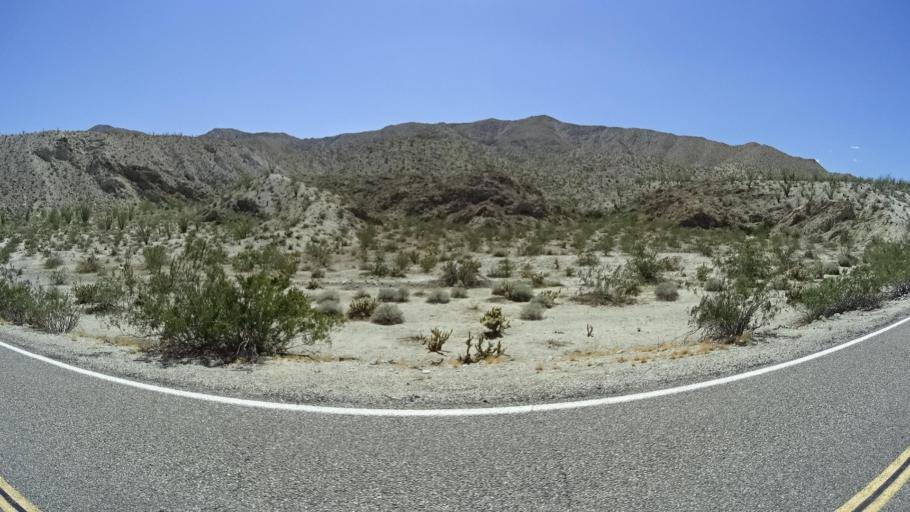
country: US
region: California
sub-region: San Diego County
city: Borrego Springs
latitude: 33.1310
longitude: -116.3030
